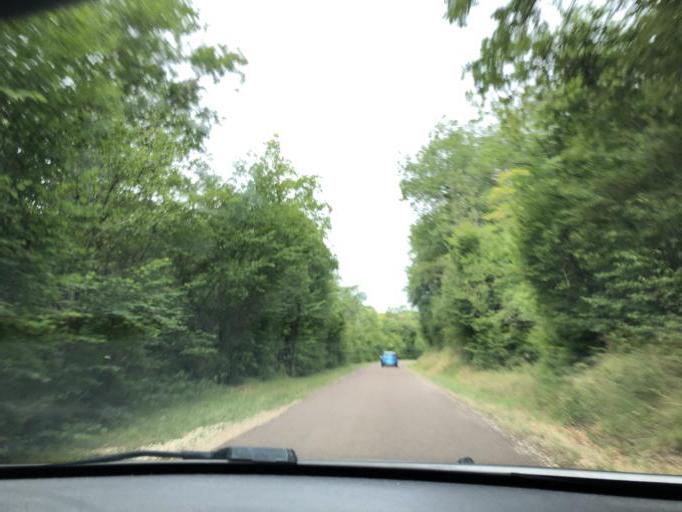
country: FR
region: Bourgogne
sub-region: Departement de l'Yonne
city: Chablis
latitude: 47.7780
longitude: 3.8243
